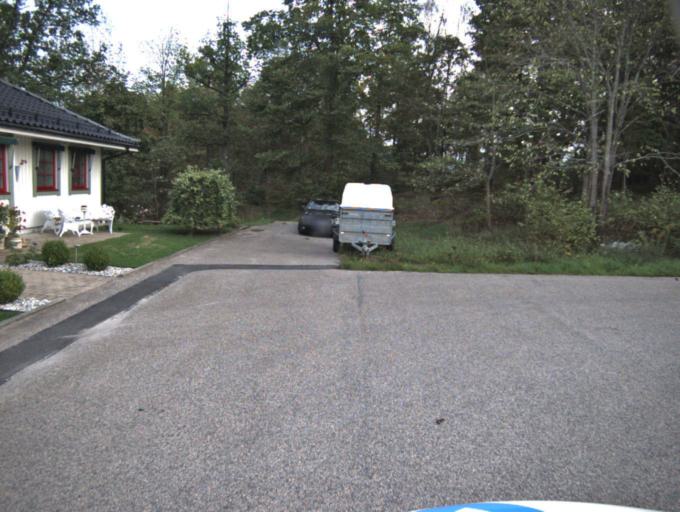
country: SE
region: Vaestra Goetaland
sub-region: Ulricehamns Kommun
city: Ulricehamn
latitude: 57.8007
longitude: 13.4258
